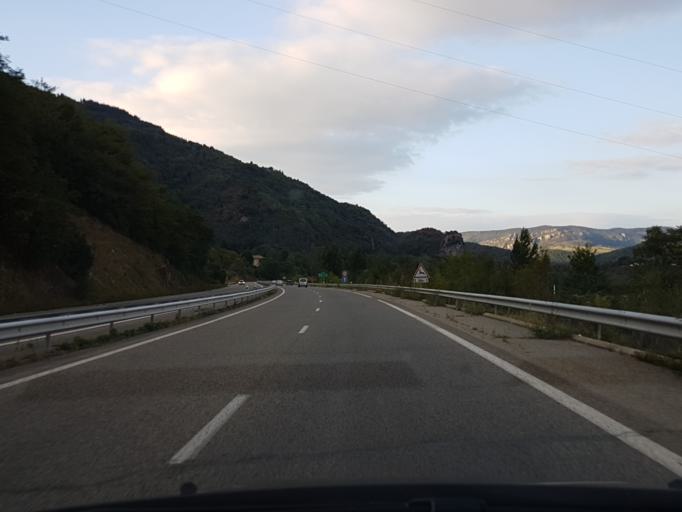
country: FR
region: Midi-Pyrenees
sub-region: Departement de l'Ariege
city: Mercus-Garrabet
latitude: 42.8779
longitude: 1.6227
